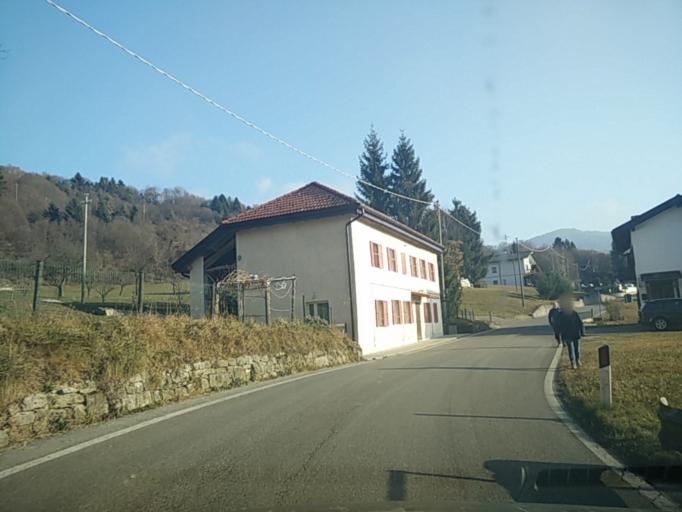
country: IT
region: Veneto
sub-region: Provincia di Belluno
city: Trichiana
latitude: 46.0489
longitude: 12.1538
